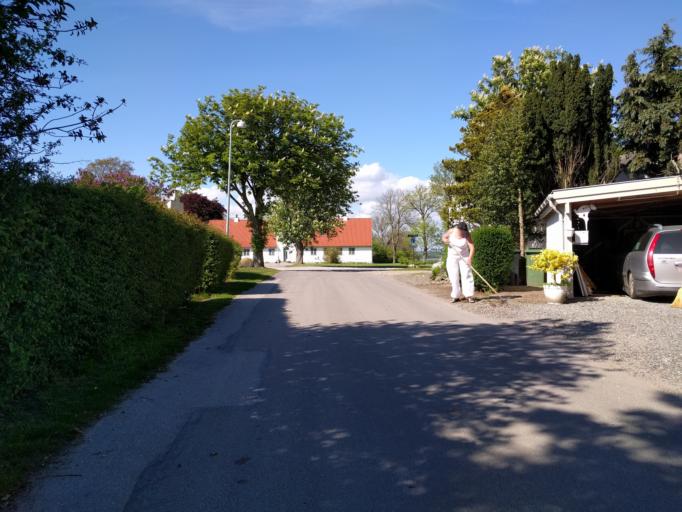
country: DK
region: Zealand
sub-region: Guldborgsund Kommune
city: Stubbekobing
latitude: 54.9316
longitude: 12.0484
